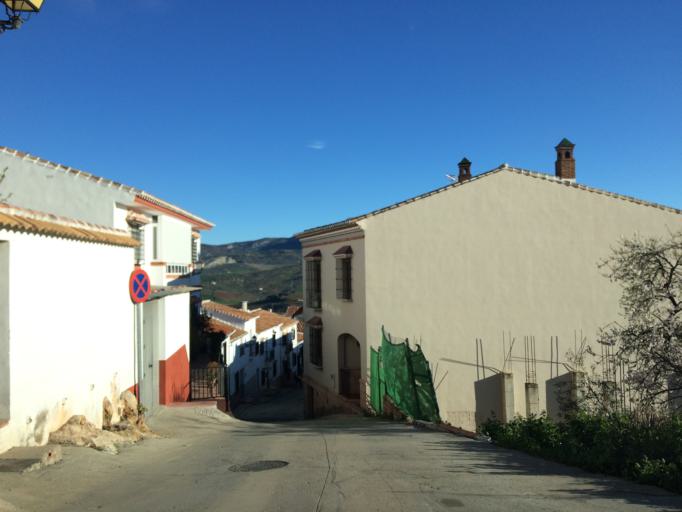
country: ES
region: Andalusia
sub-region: Provincia de Malaga
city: Casabermeja
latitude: 36.8909
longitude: -4.4285
